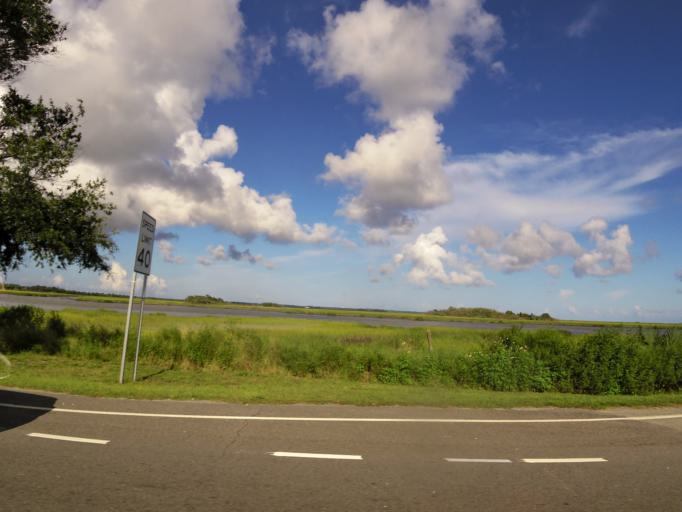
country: US
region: Georgia
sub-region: Glynn County
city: Brunswick
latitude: 31.1543
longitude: -81.4789
